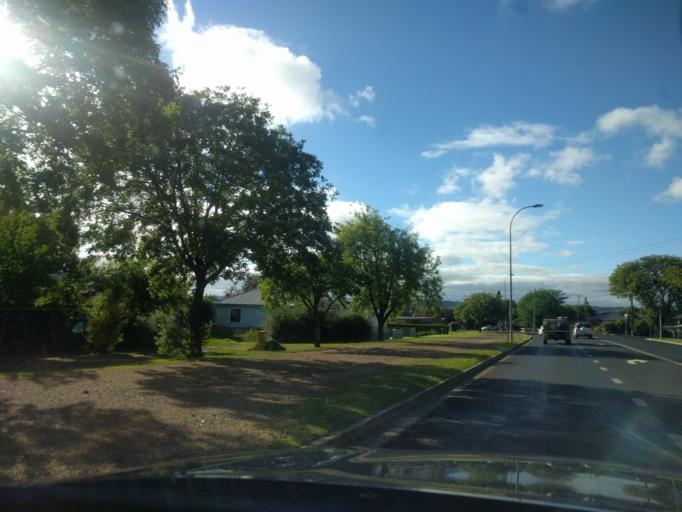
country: AU
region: New South Wales
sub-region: Armidale Dumaresq
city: Armidale
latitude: -30.5015
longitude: 151.6707
